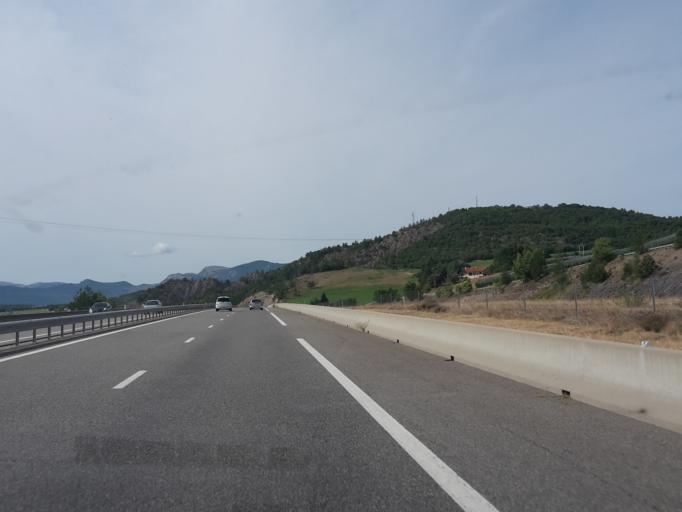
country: FR
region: Provence-Alpes-Cote d'Azur
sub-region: Departement des Hautes-Alpes
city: Laragne-Monteglin
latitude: 44.3418
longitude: 5.9039
